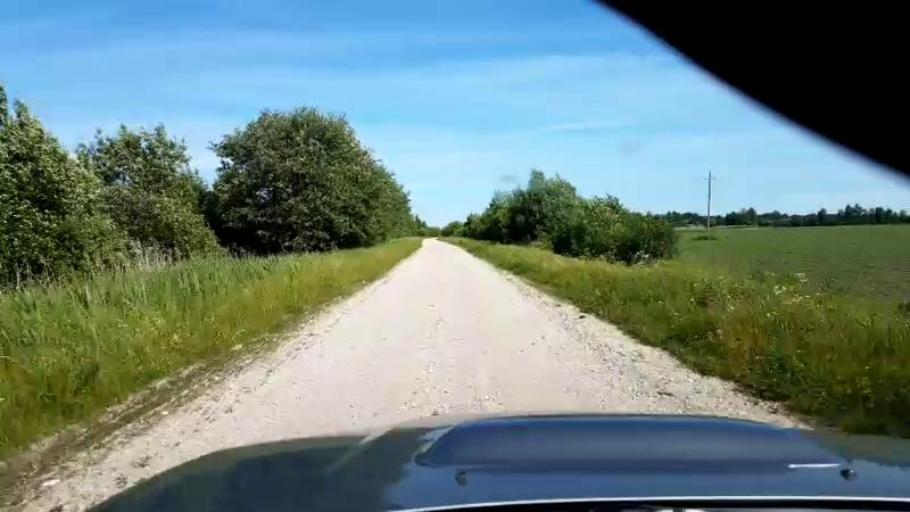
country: EE
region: Paernumaa
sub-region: Sauga vald
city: Sauga
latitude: 58.4705
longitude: 24.5335
